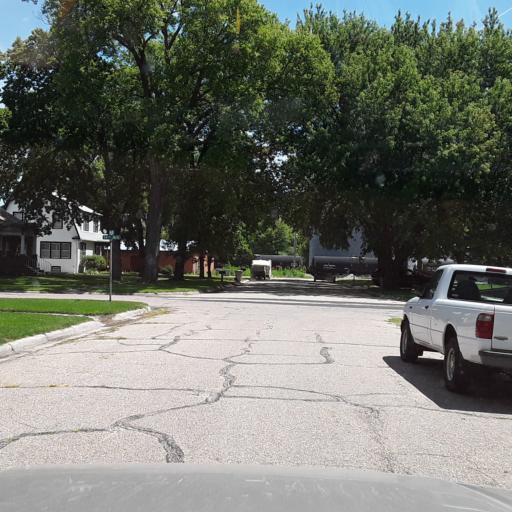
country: US
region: Nebraska
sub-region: Merrick County
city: Central City
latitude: 41.1172
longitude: -97.9980
